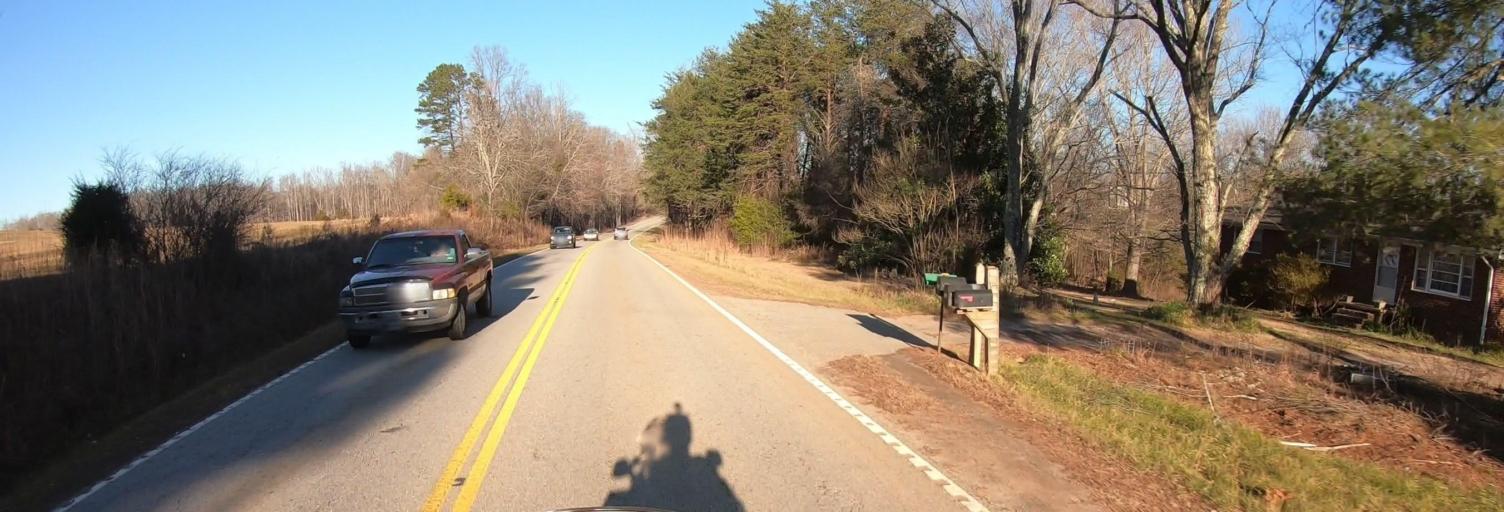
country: US
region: South Carolina
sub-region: Spartanburg County
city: Landrum
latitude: 35.1326
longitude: -82.1180
